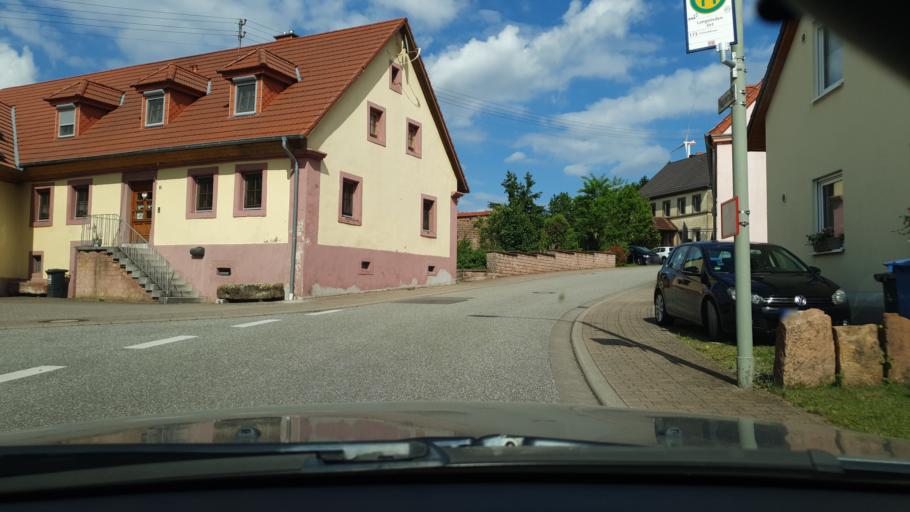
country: DE
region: Rheinland-Pfalz
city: Langwieden
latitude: 49.3752
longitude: 7.4997
